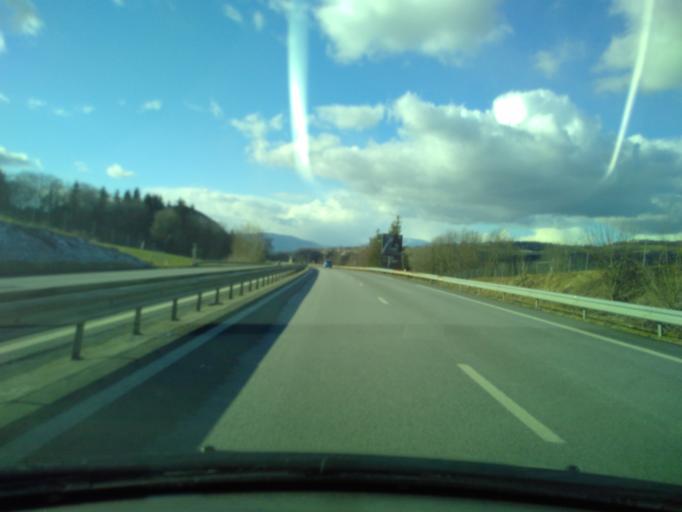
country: FR
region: Rhone-Alpes
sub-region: Departement de la Haute-Savoie
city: Allonzier-la-Caille
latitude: 46.0022
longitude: 6.1444
